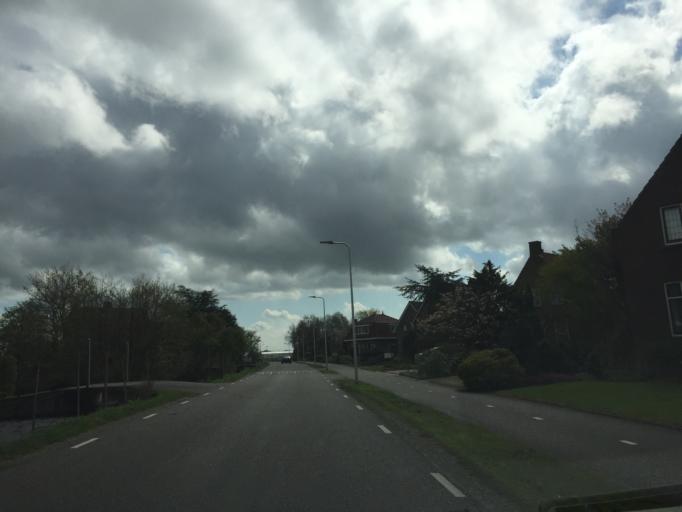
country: NL
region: South Holland
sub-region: Gemeente Boskoop
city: Boskoop
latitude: 52.0869
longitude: 4.6280
